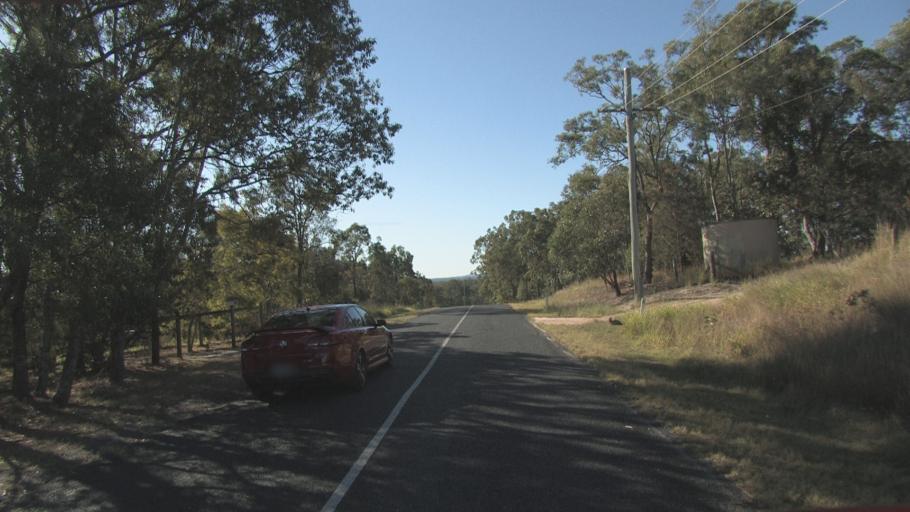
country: AU
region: Queensland
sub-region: Logan
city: Logan Reserve
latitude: -27.7267
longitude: 153.1052
